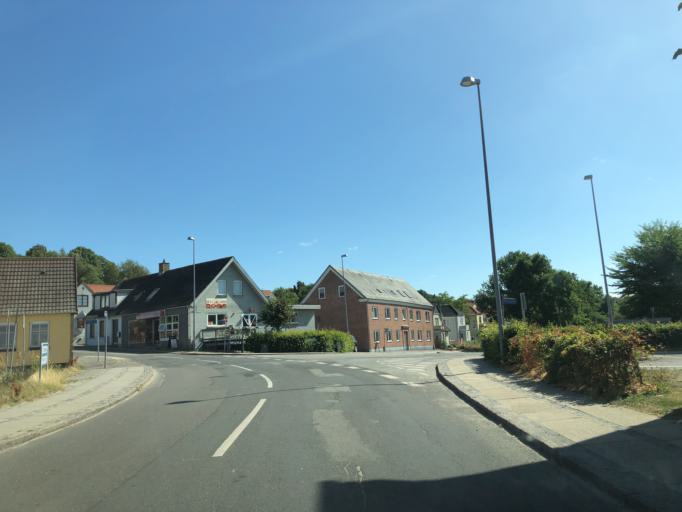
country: DK
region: North Denmark
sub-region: Mariagerfjord Kommune
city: Hobro
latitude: 56.6357
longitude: 9.7928
